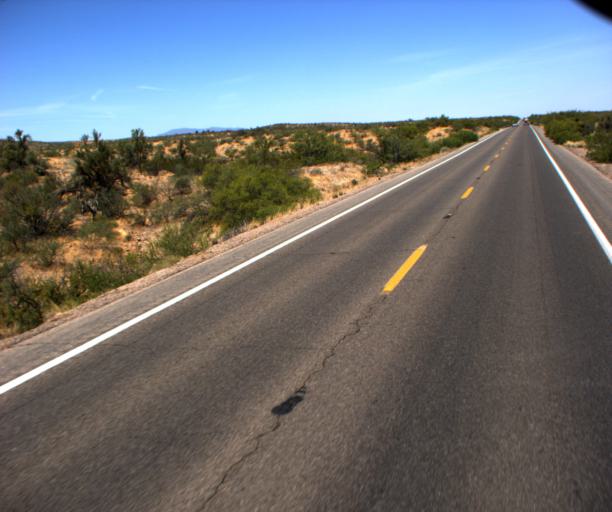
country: US
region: Arizona
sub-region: Gila County
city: Peridot
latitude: 33.3262
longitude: -110.5549
